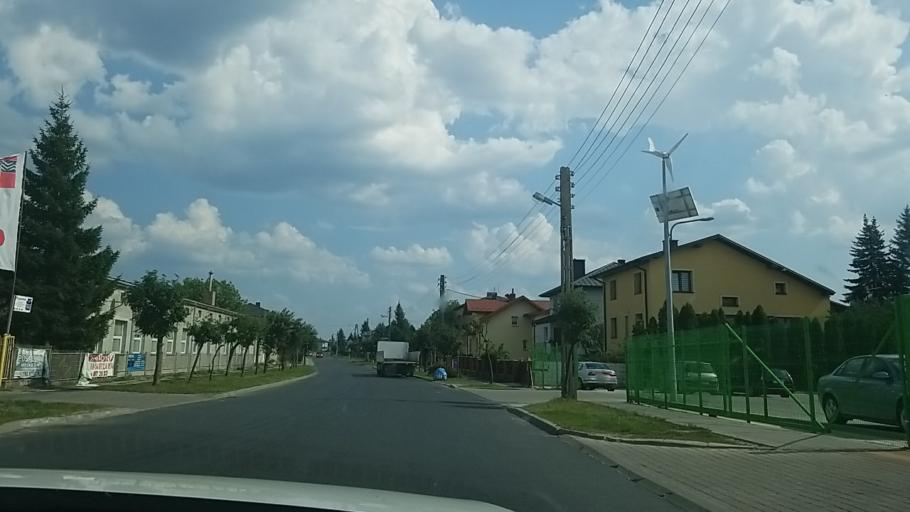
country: PL
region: Lublin Voivodeship
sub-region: Powiat janowski
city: Janow Lubelski
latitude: 50.7056
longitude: 22.4055
